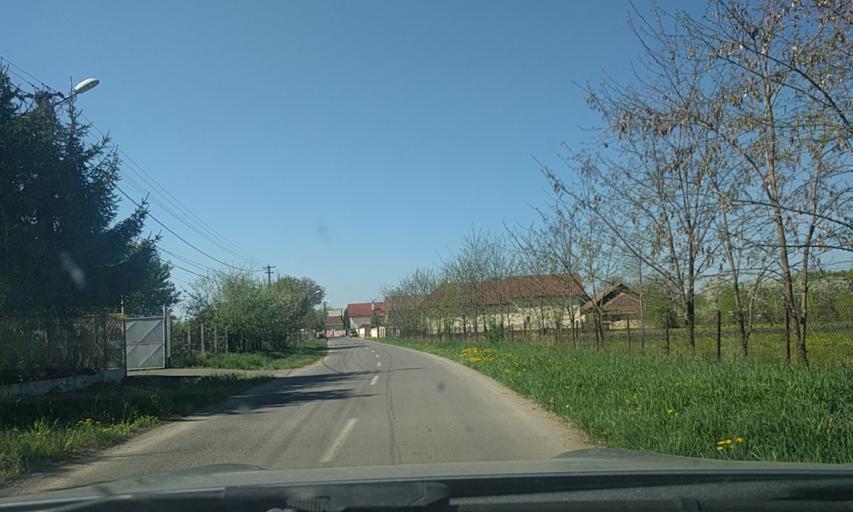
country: RO
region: Brasov
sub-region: Comuna Bod
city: Colonia Bod
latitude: 45.7110
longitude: 25.5770
